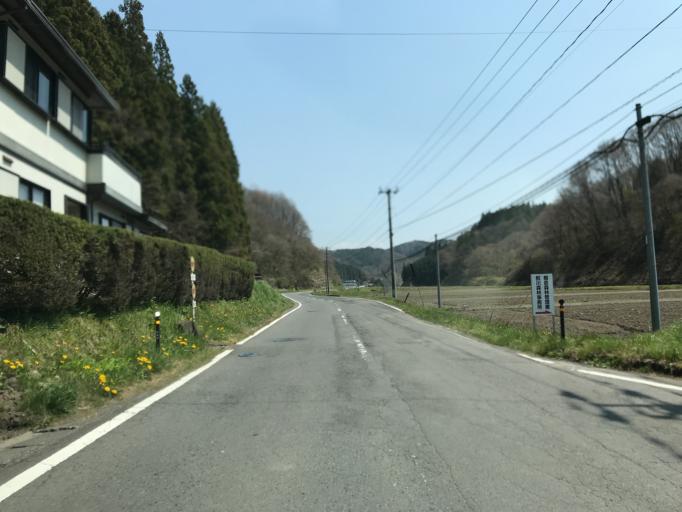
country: JP
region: Fukushima
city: Ishikawa
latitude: 37.0468
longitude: 140.4955
